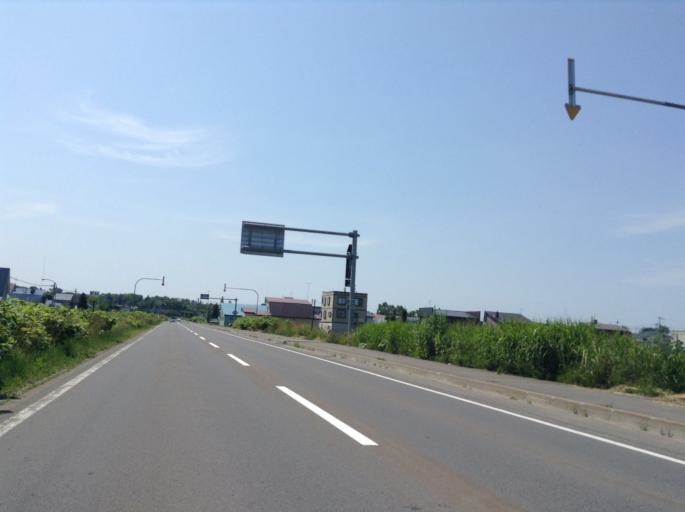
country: JP
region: Hokkaido
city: Nayoro
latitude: 44.3560
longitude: 142.4733
